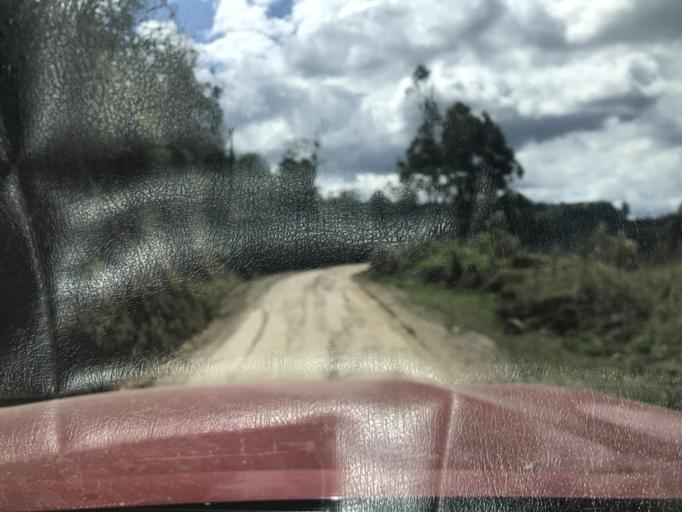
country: PE
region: Cajamarca
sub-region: Provincia de Chota
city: Querocoto
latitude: -6.3501
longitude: -79.0373
